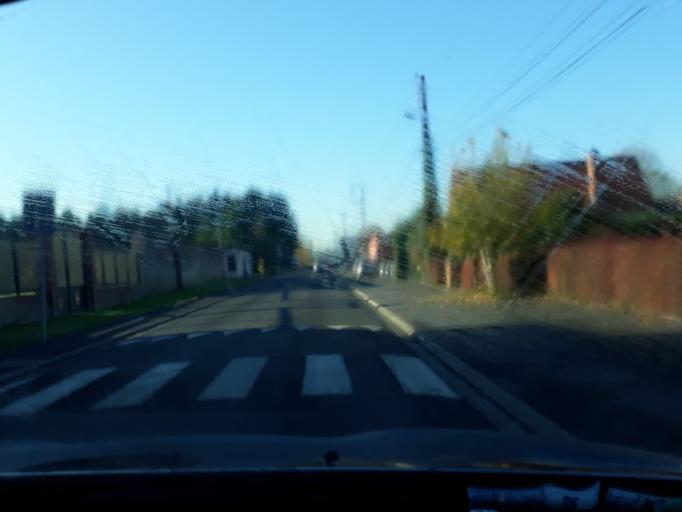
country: FR
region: Nord-Pas-de-Calais
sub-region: Departement du Nord
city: Masny
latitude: 50.3458
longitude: 3.1958
